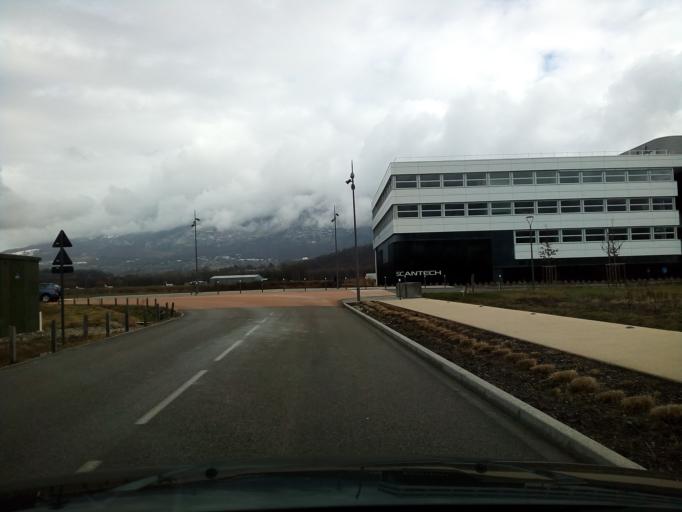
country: FR
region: Rhone-Alpes
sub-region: Departement de la Savoie
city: Le Bourget-du-Lac
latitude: 45.6376
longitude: 5.8750
